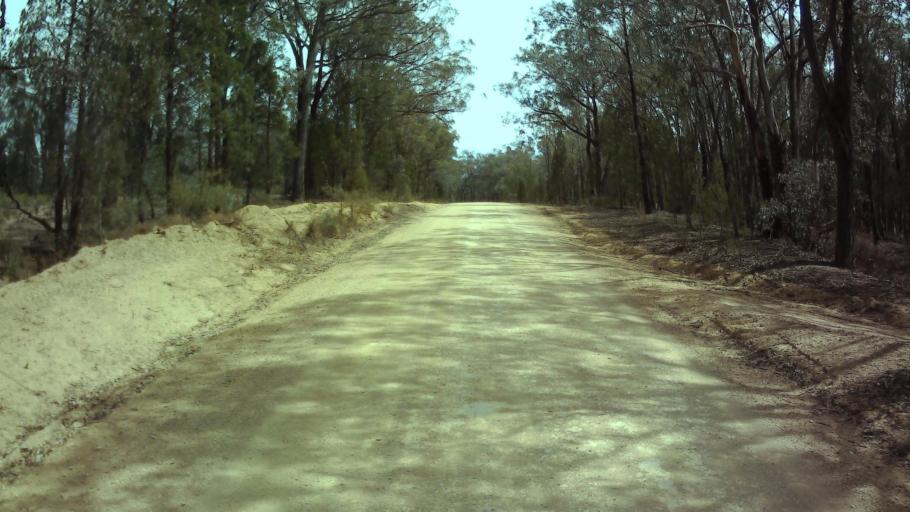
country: AU
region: New South Wales
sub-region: Weddin
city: Grenfell
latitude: -33.9068
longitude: 148.4092
